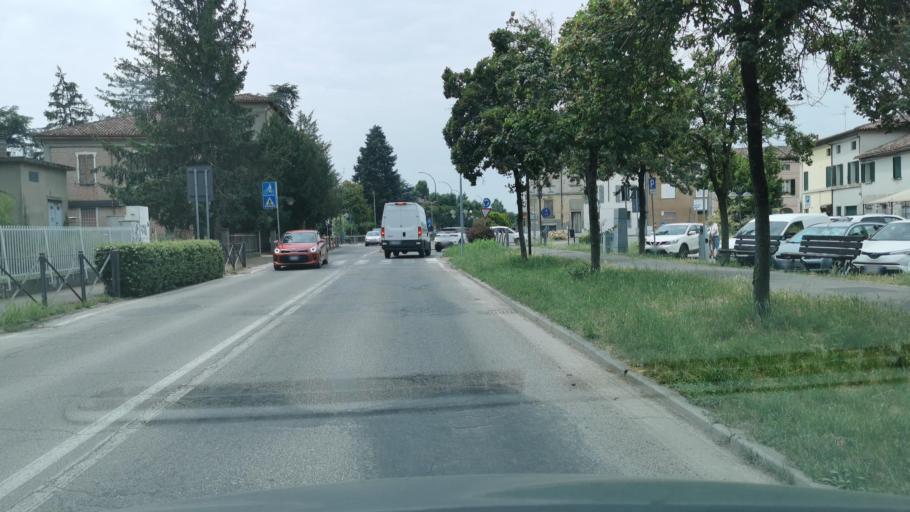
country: IT
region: Emilia-Romagna
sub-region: Provincia di Ravenna
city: Bagnacavallo
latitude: 44.4160
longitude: 11.9806
